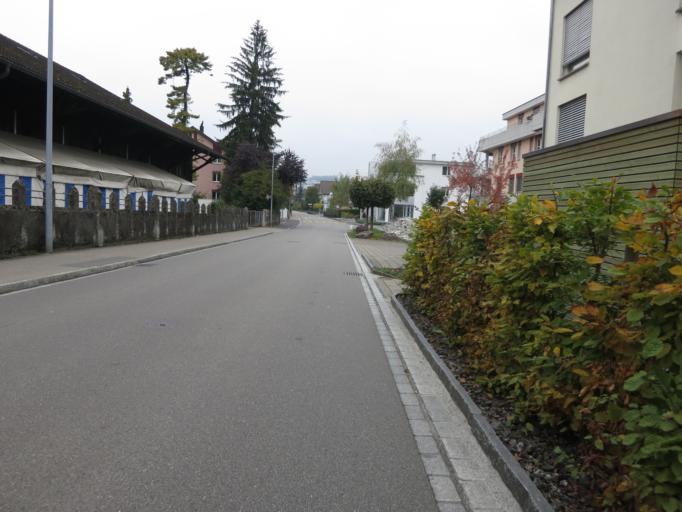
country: CH
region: Saint Gallen
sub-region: Wahlkreis See-Gaster
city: Rapperswil
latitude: 47.2297
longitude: 8.8243
